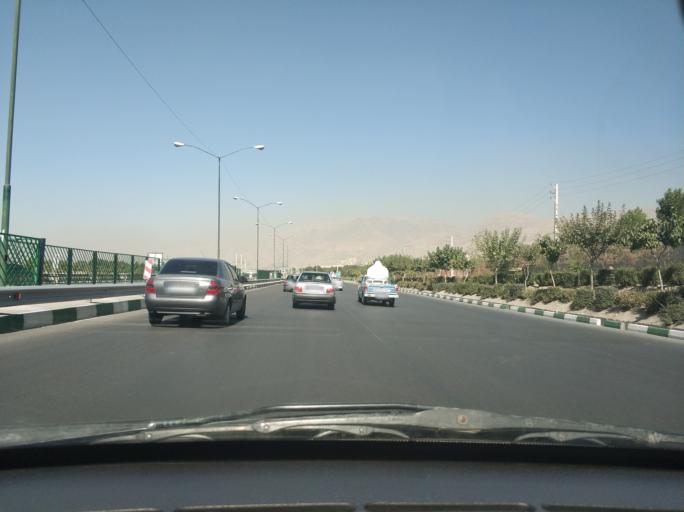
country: IR
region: Tehran
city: Tajrish
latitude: 35.7674
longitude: 51.5620
